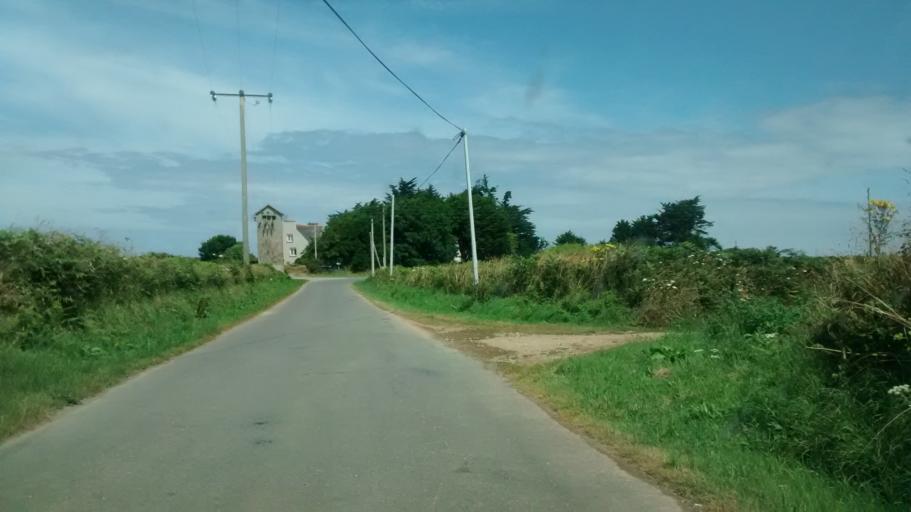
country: FR
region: Brittany
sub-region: Departement du Finistere
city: Plouguerneau
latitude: 48.6150
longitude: -4.4803
